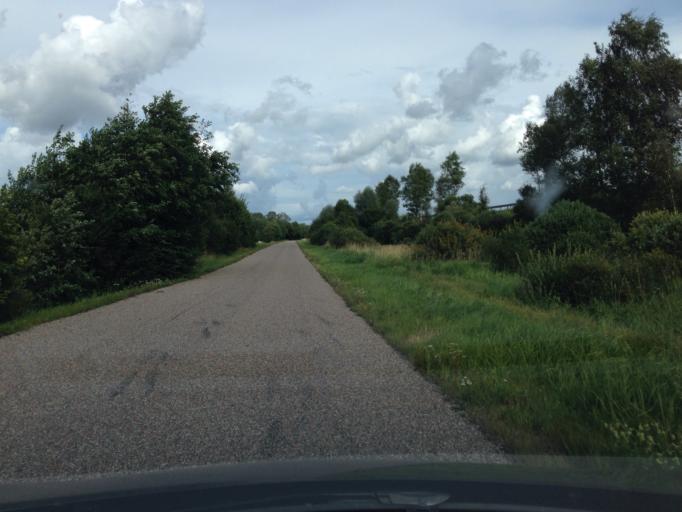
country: EE
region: Harju
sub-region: Saue linn
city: Saue
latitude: 59.2703
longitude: 24.5175
